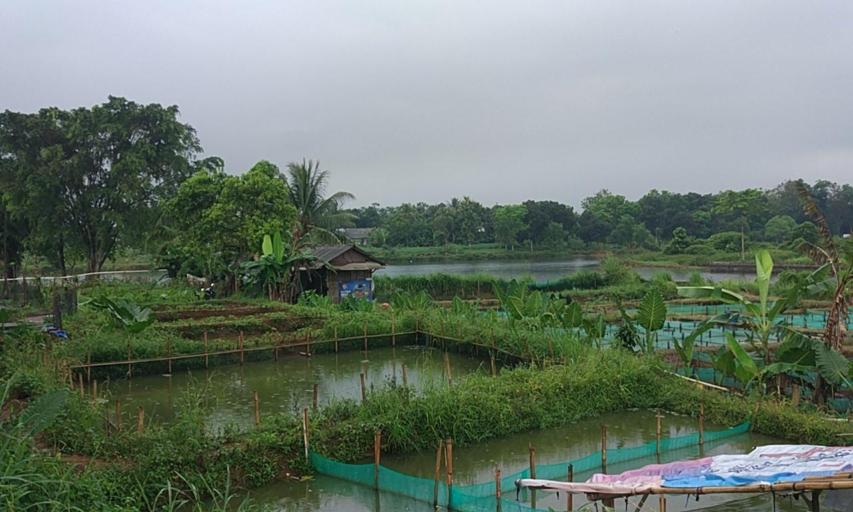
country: ID
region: West Java
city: Parung
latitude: -6.4946
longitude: 106.7631
